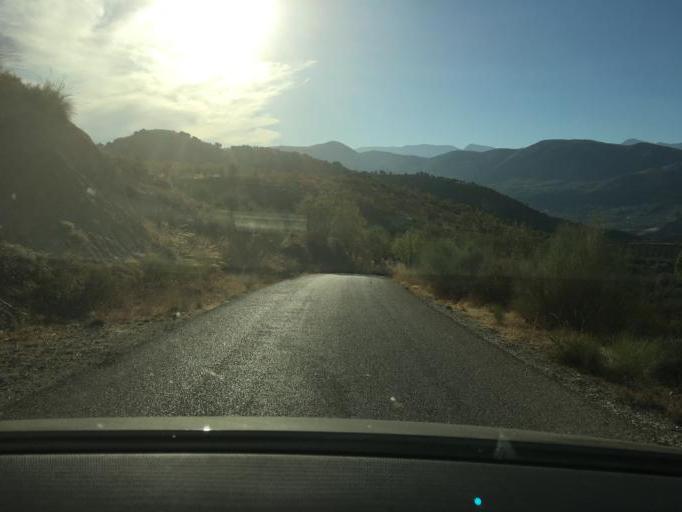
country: ES
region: Andalusia
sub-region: Provincia de Granada
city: Beas de Granada
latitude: 37.2144
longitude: -3.4718
